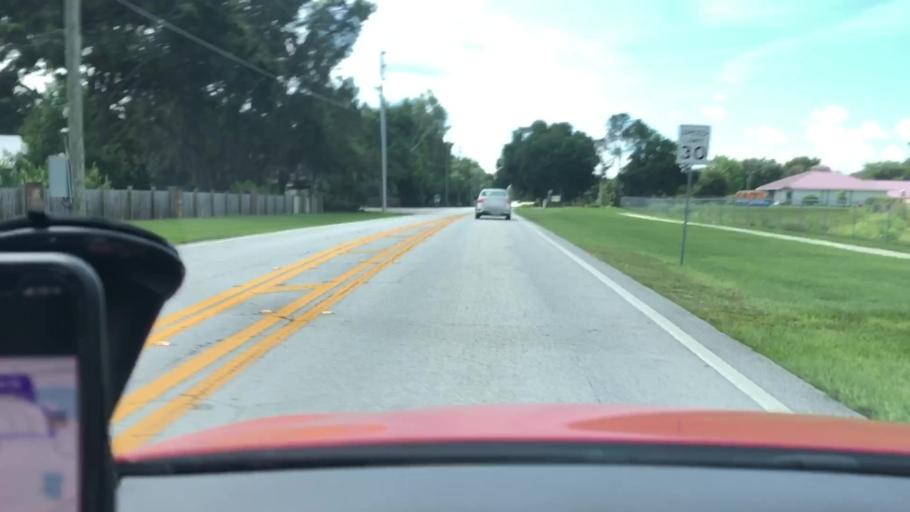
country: US
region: Florida
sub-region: Lake County
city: Eustis
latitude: 28.8470
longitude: -81.6546
